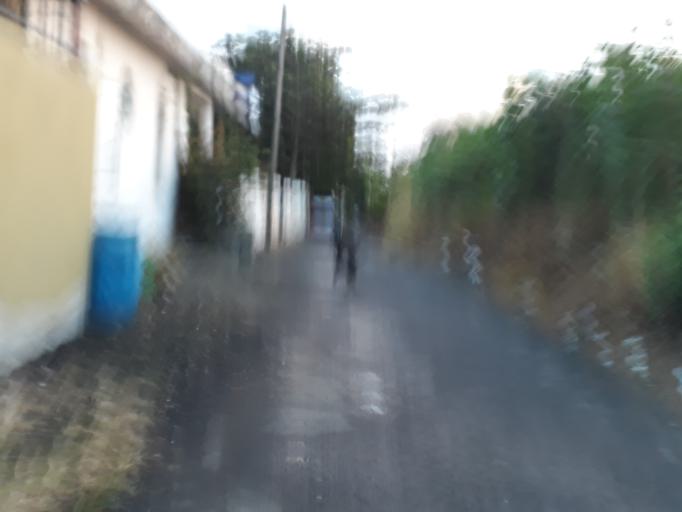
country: MU
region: Riviere du Rempart
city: Grand Baie
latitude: -20.0184
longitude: 57.5807
